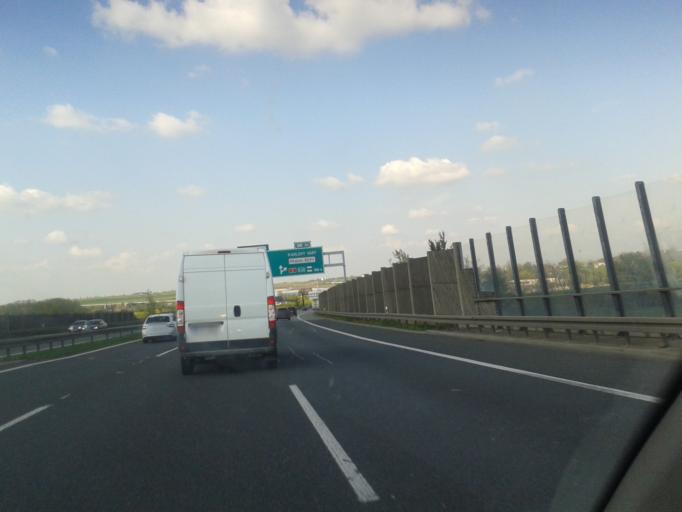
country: CZ
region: Central Bohemia
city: Hostivice
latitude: 50.0631
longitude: 14.2776
